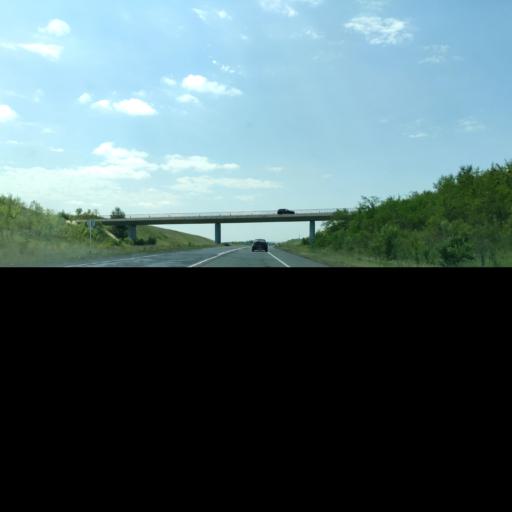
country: RU
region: Samara
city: Petra-Dubrava
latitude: 53.3008
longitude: 50.4090
